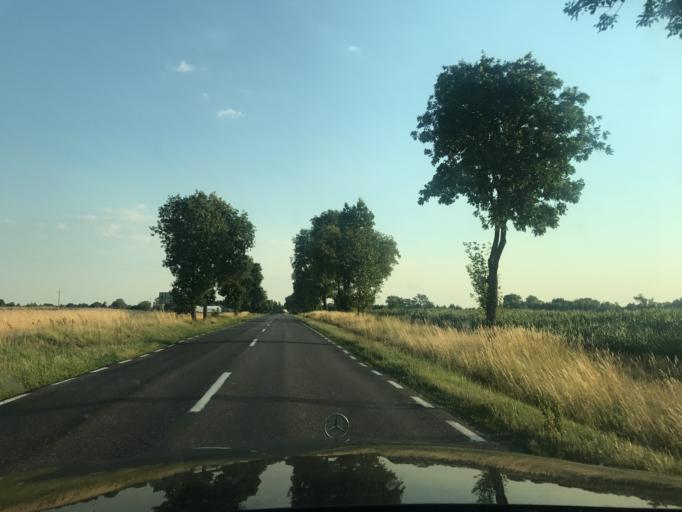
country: PL
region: Lublin Voivodeship
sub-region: Powiat parczewski
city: Debowa Kloda
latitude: 51.6585
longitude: 23.0031
